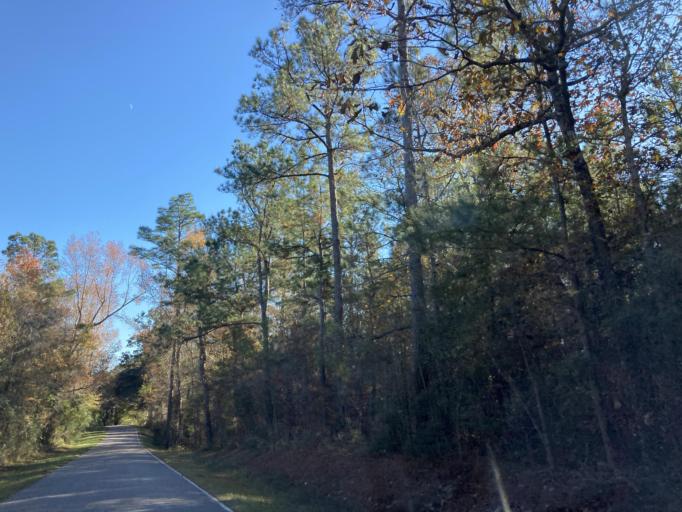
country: US
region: Mississippi
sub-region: Lamar County
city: Sumrall
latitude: 31.3695
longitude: -89.5794
